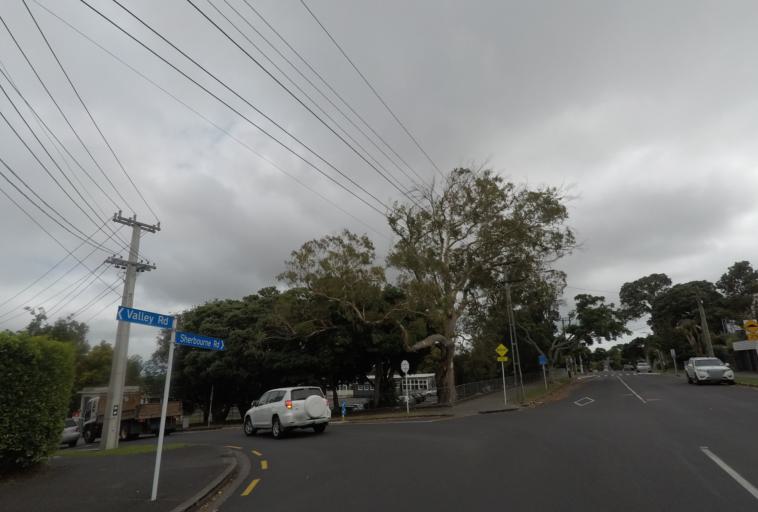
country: NZ
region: Auckland
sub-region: Auckland
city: Auckland
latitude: -36.8776
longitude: 174.7572
